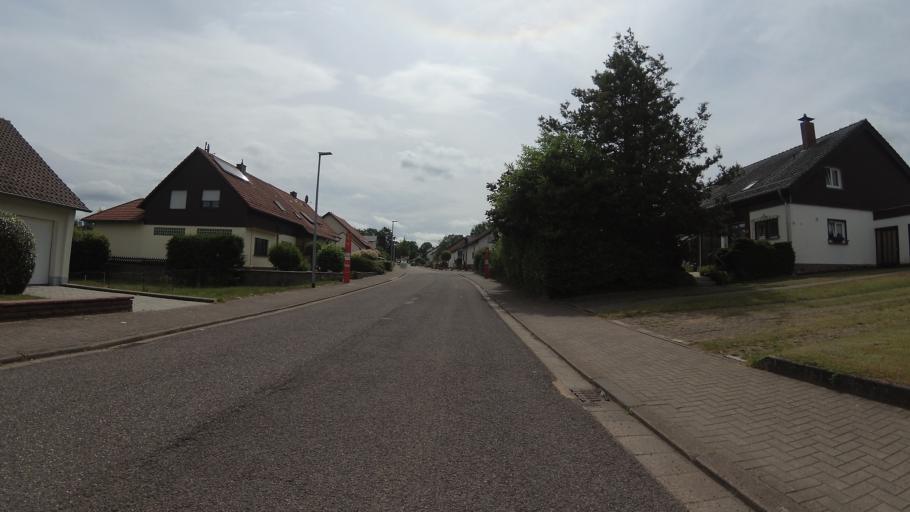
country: DE
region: Saarland
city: Sankt Ingbert
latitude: 49.2787
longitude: 7.1679
